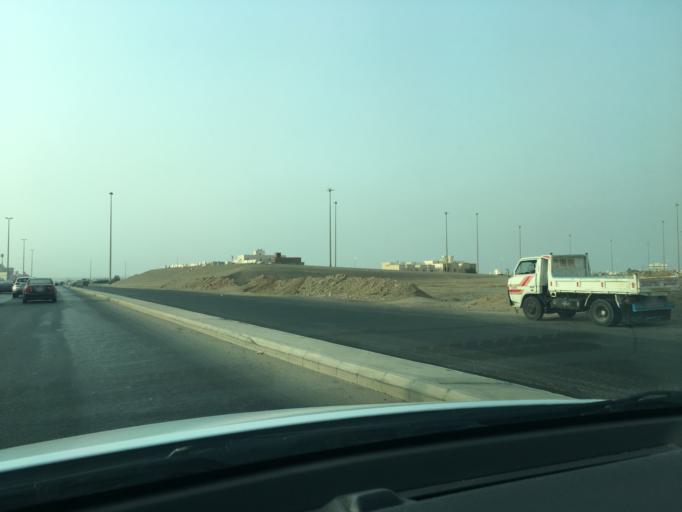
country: SA
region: Makkah
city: Jeddah
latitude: 21.7621
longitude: 39.1833
